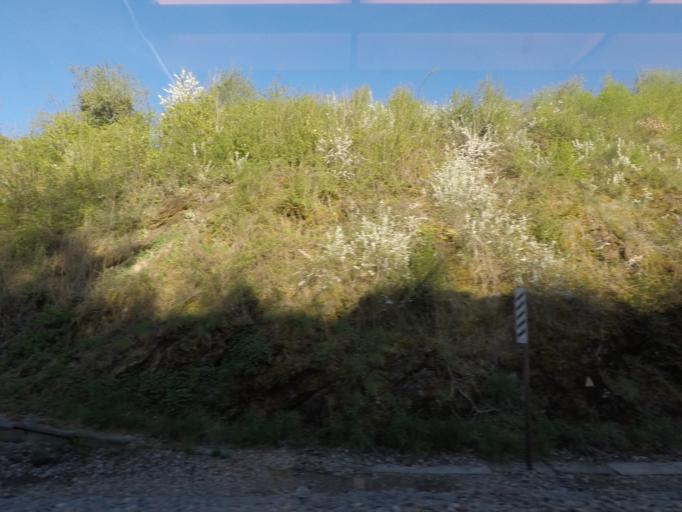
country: BE
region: Wallonia
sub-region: Province du Luxembourg
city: Tellin
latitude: 50.0918
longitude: 5.2816
